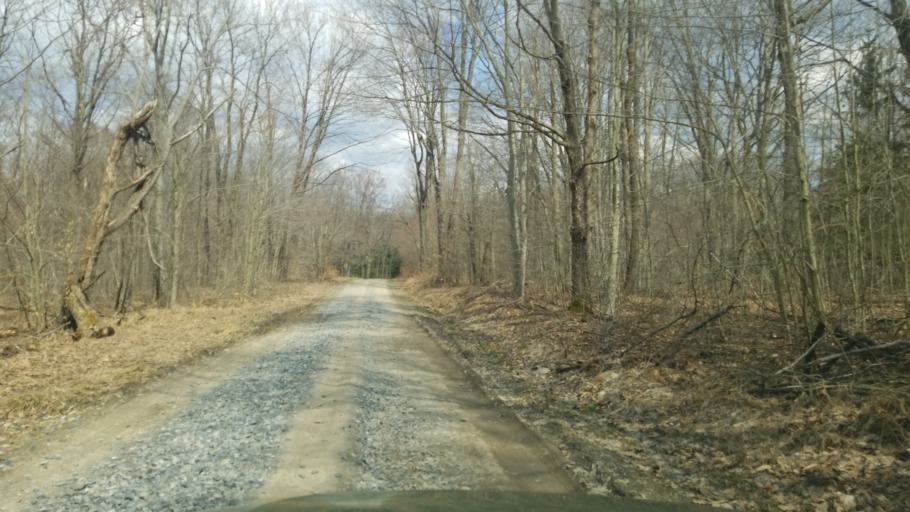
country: US
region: Pennsylvania
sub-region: Clearfield County
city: Clearfield
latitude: 41.1575
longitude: -78.5150
